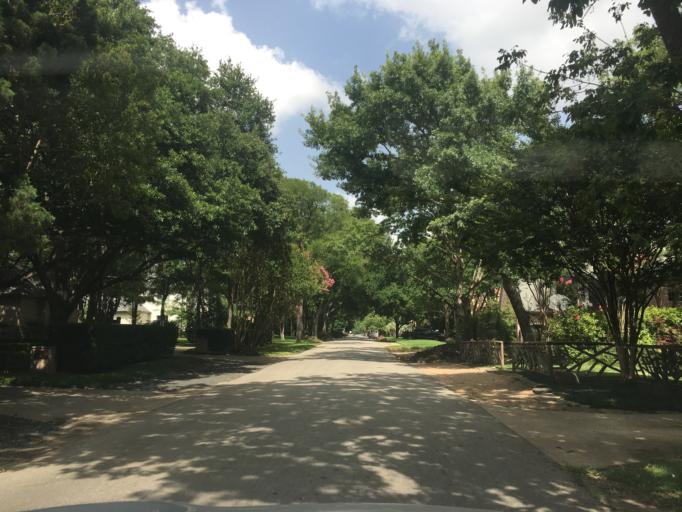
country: US
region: Texas
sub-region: Dallas County
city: University Park
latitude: 32.8843
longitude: -96.7996
